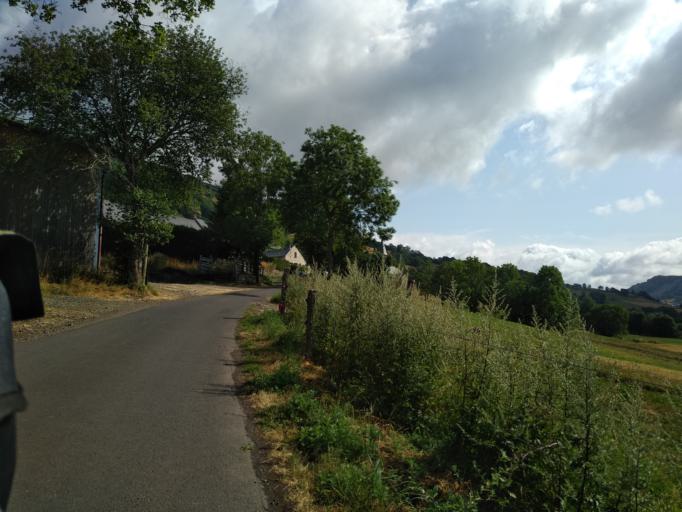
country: FR
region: Auvergne
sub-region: Departement du Cantal
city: Murat
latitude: 45.1367
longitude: 2.7470
